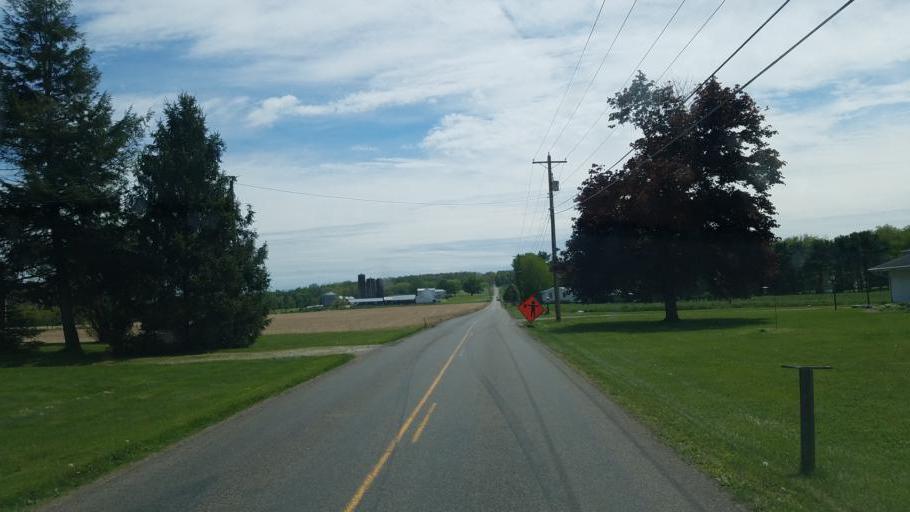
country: US
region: Ohio
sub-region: Knox County
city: Gambier
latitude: 40.4069
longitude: -82.3691
